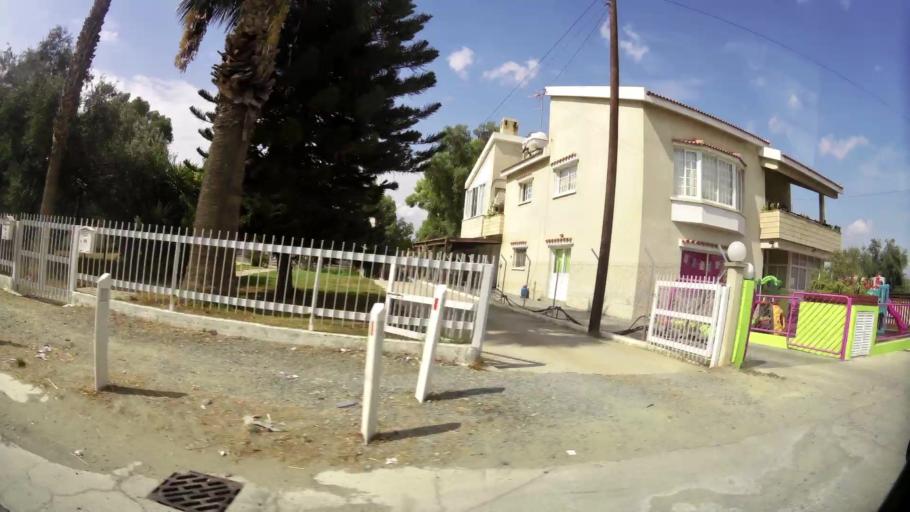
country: CY
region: Lefkosia
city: Tseri
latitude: 35.0829
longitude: 33.3284
